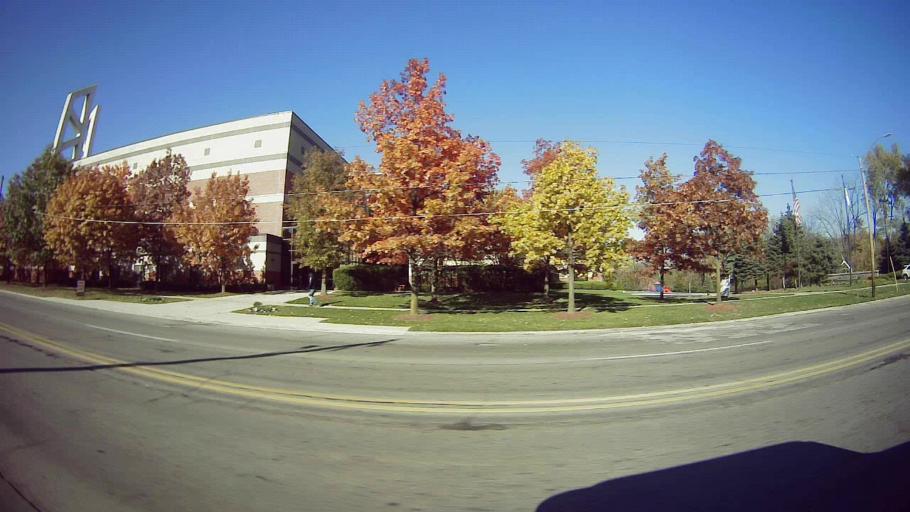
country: US
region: Michigan
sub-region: Wayne County
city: Redford
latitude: 42.4291
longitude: -83.2703
